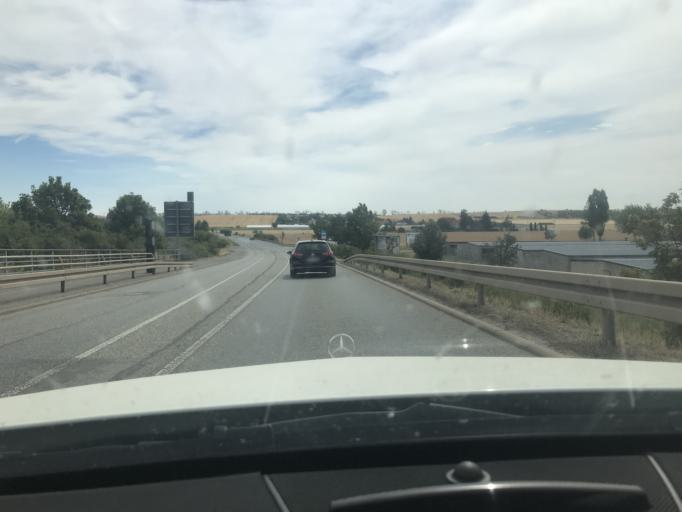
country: DE
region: Thuringia
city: Erfurt
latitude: 51.0116
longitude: 11.0447
